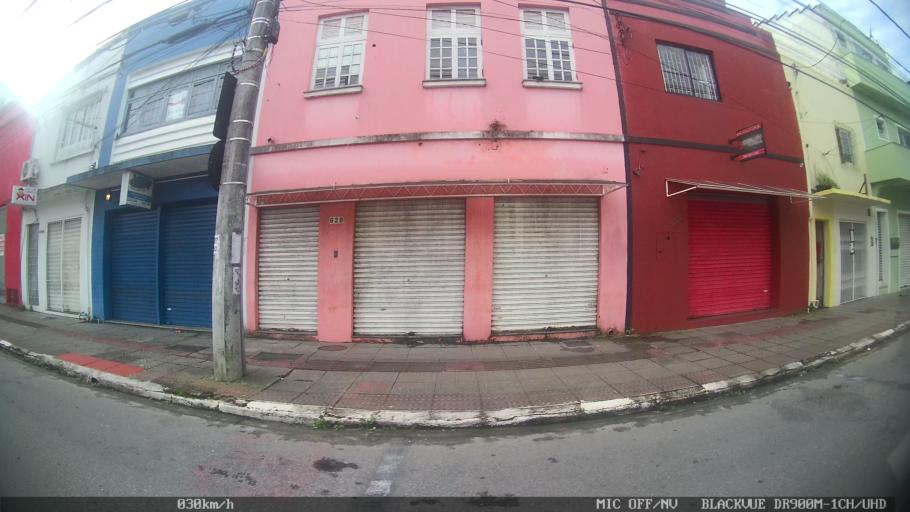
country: BR
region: Santa Catarina
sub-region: Florianopolis
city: Florianopolis
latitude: -27.5956
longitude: -48.5560
